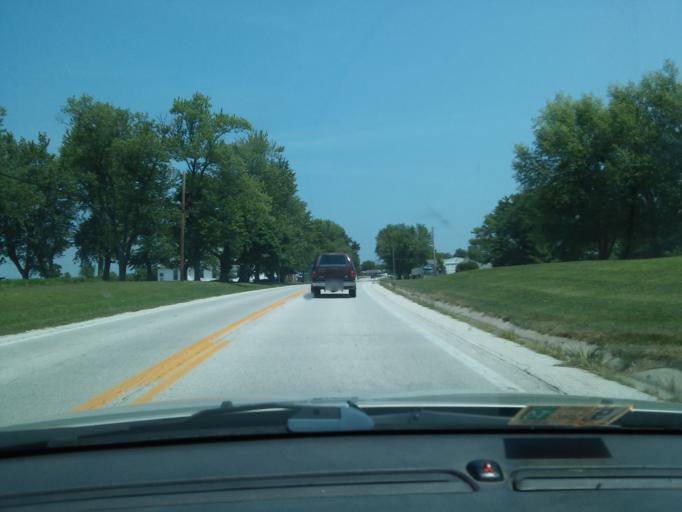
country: US
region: Illinois
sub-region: Pike County
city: Pittsfield
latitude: 39.5725
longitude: -90.9127
